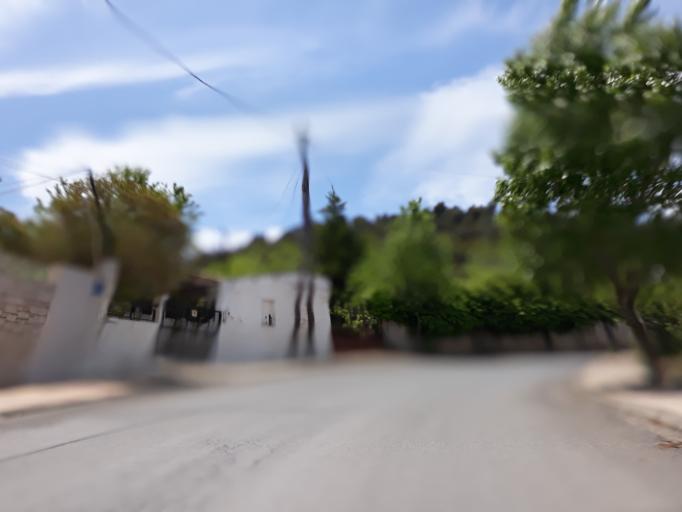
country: GR
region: Attica
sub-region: Nomarchia Dytikis Attikis
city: Magoula
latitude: 38.1730
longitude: 23.5468
